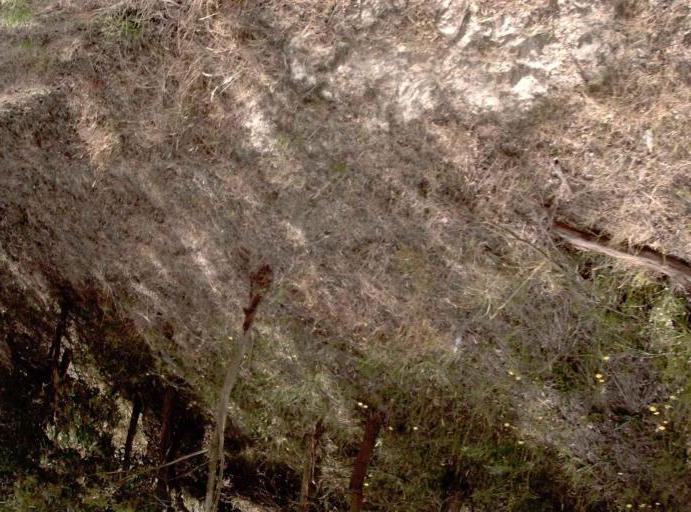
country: AU
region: Victoria
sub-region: Latrobe
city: Traralgon
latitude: -38.2971
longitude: 146.7028
